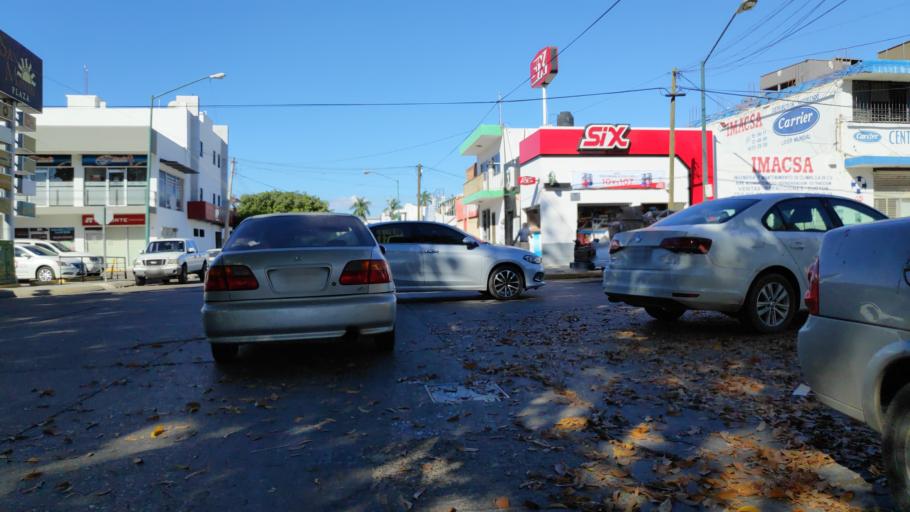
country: MX
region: Sinaloa
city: Culiacan
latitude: 24.8000
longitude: -107.3965
